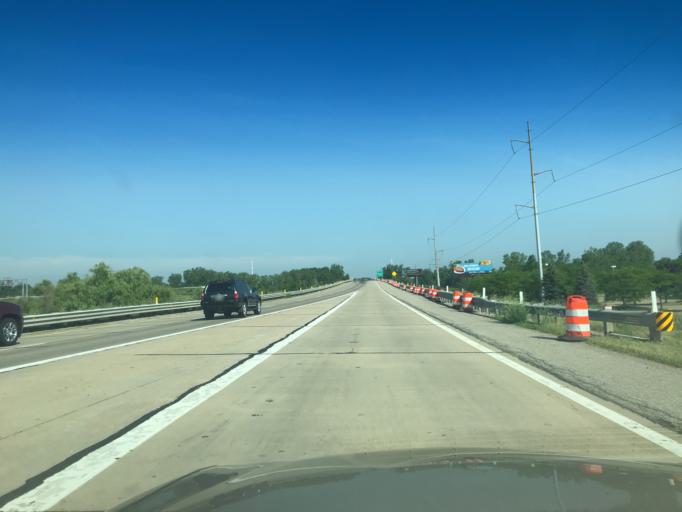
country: US
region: Michigan
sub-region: Eaton County
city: Dimondale
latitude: 42.6802
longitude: -84.6548
